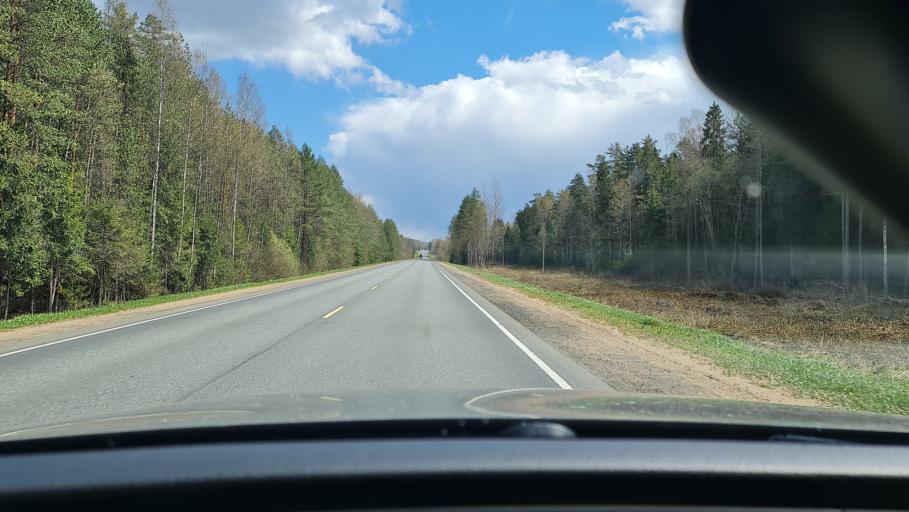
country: RU
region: Tverskaya
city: Zapadnaya Dvina
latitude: 56.3046
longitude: 32.2256
